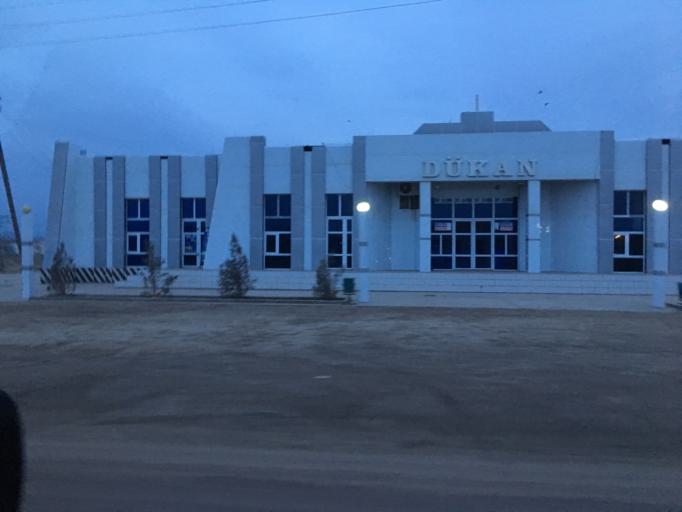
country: TM
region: Dasoguz
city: Yylanly
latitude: 41.8836
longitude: 59.6239
